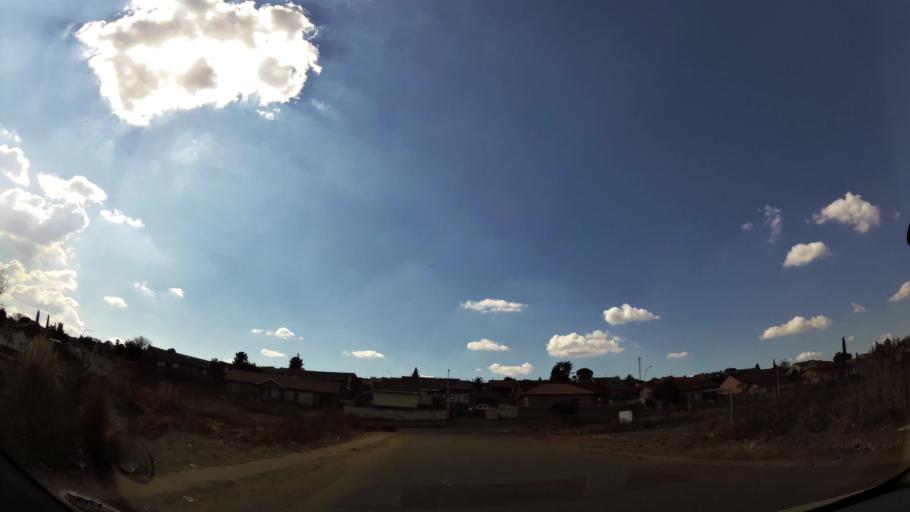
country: ZA
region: Mpumalanga
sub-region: Nkangala District Municipality
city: Witbank
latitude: -25.9349
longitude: 29.2446
